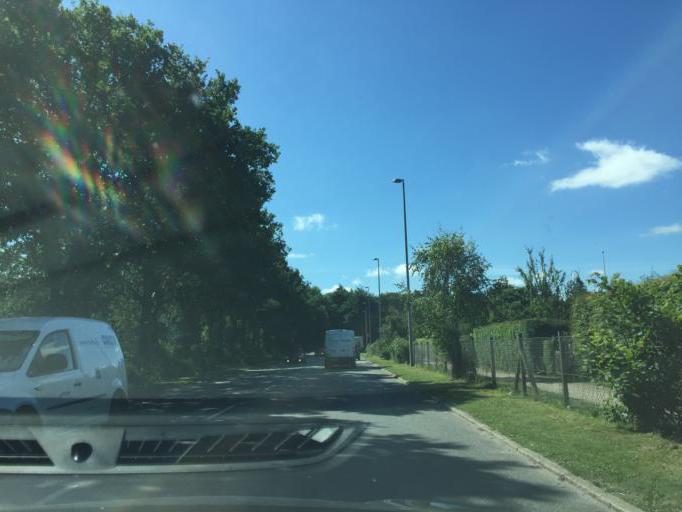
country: DK
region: South Denmark
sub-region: Odense Kommune
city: Odense
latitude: 55.3917
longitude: 10.3650
